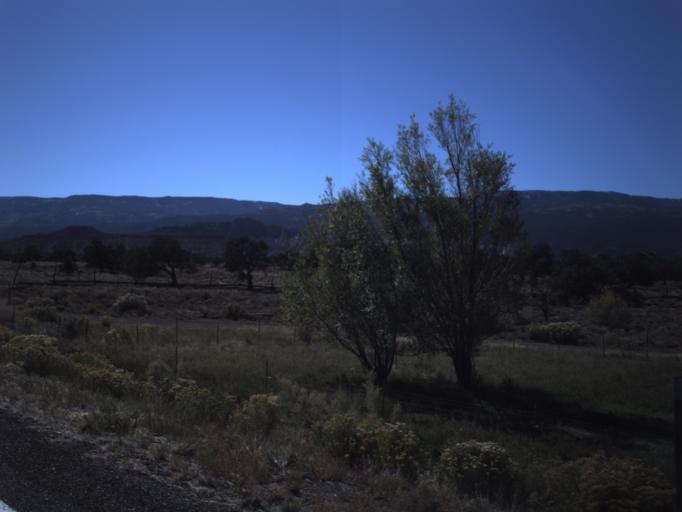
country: US
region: Utah
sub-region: Wayne County
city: Loa
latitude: 38.2963
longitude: -111.4013
